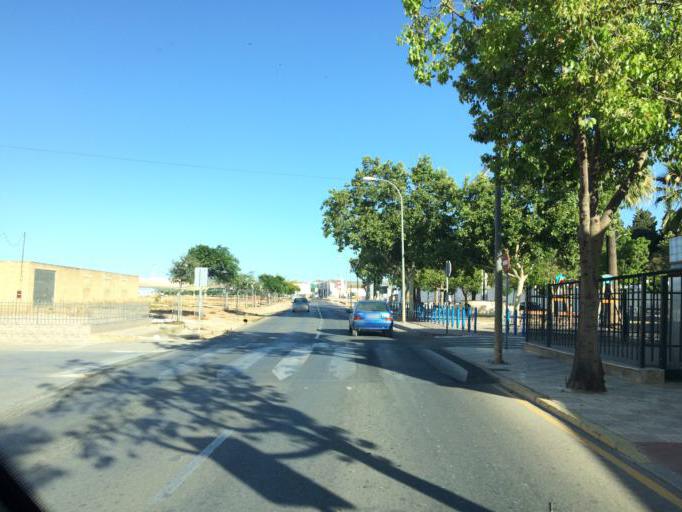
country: ES
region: Andalusia
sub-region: Provincia de Malaga
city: Campillos
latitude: 37.0485
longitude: -4.8676
